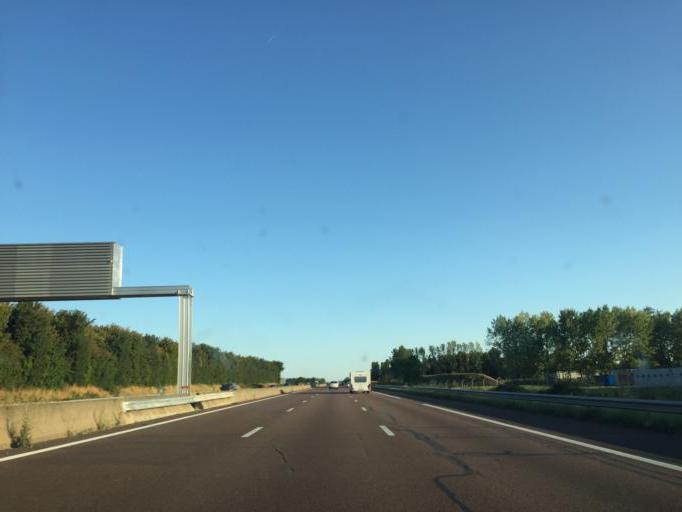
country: FR
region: Bourgogne
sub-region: Departement de Saone-et-Loire
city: Sevrey
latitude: 46.7314
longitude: 4.8361
